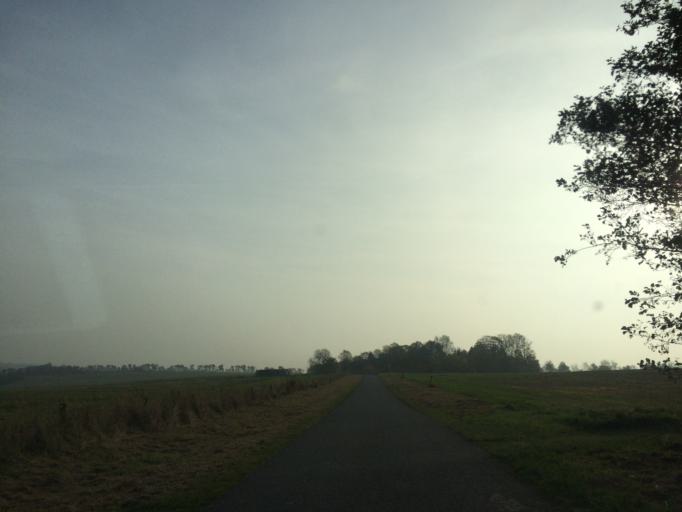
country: DK
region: Central Jutland
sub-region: Silkeborg Kommune
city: Svejbaek
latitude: 56.2394
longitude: 9.7021
